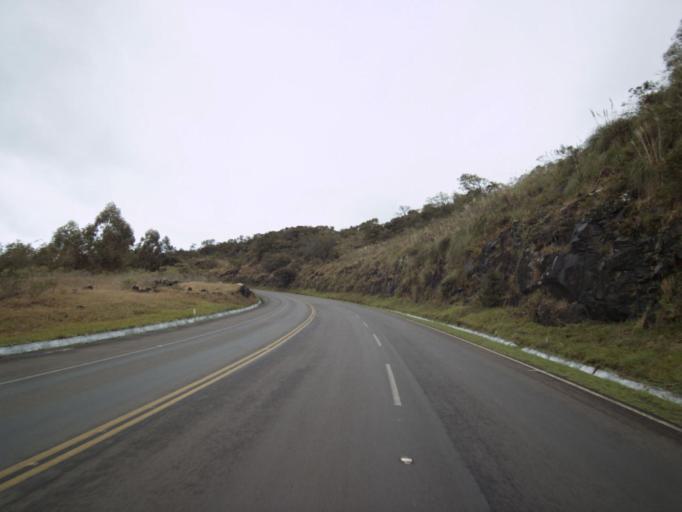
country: BR
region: Santa Catarina
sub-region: Concordia
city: Concordia
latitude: -27.0563
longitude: -51.8900
